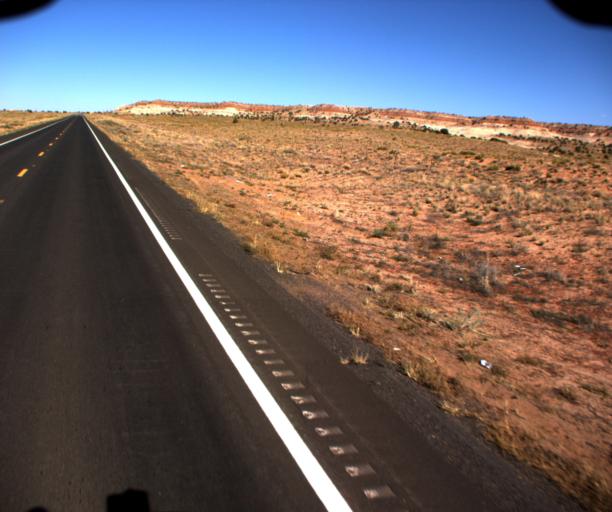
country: US
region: Arizona
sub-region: Coconino County
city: Tuba City
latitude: 36.2280
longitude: -111.0343
